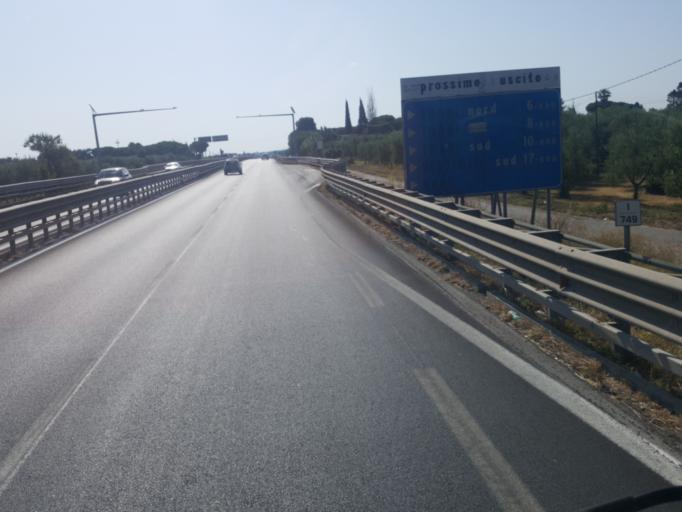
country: IT
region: Apulia
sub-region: Provincia di Barletta - Andria - Trani
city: Barletta
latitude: 41.3023
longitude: 16.3120
